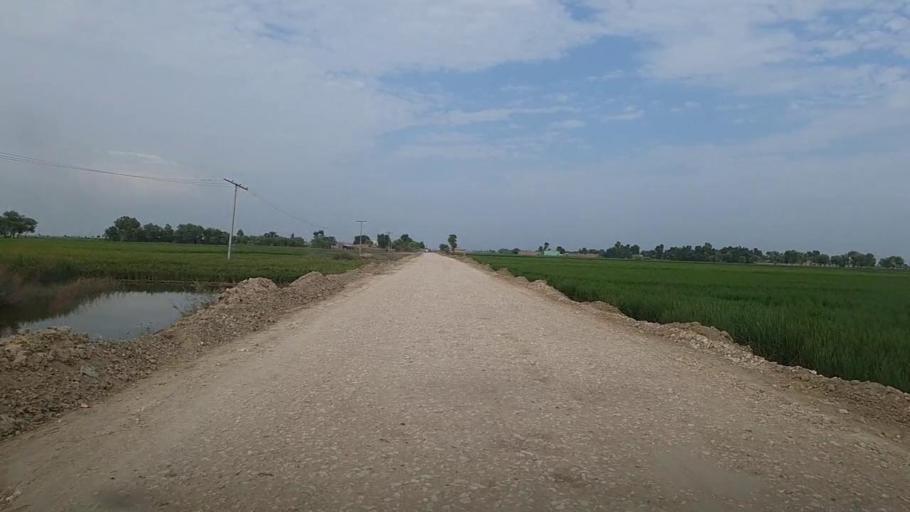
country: PK
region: Sindh
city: Thul
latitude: 28.2527
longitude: 68.8005
